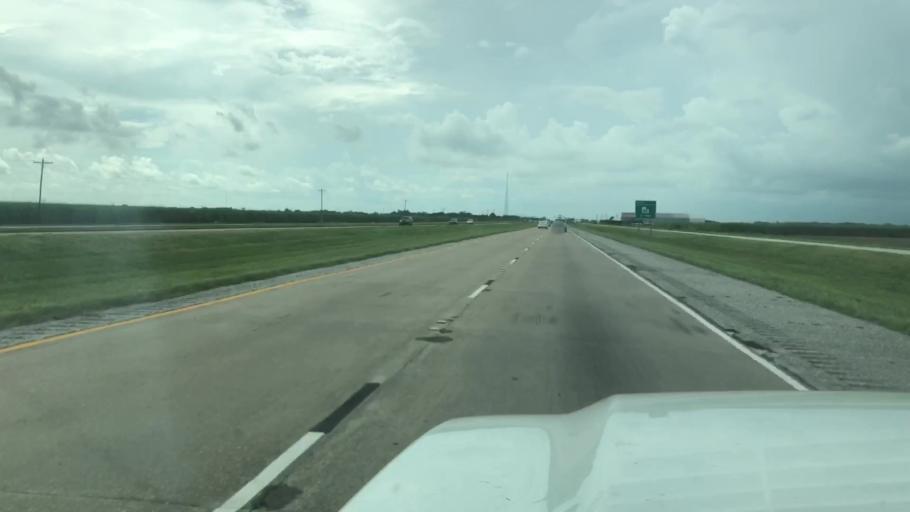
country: US
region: Louisiana
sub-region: Iberia Parish
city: Jeanerette
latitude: 29.9072
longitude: -91.7096
